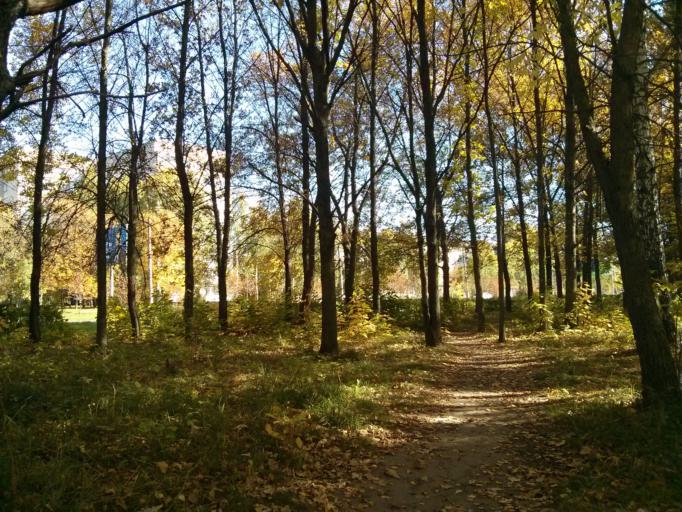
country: RU
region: Vladimir
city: Murom
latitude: 55.5498
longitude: 42.0626
